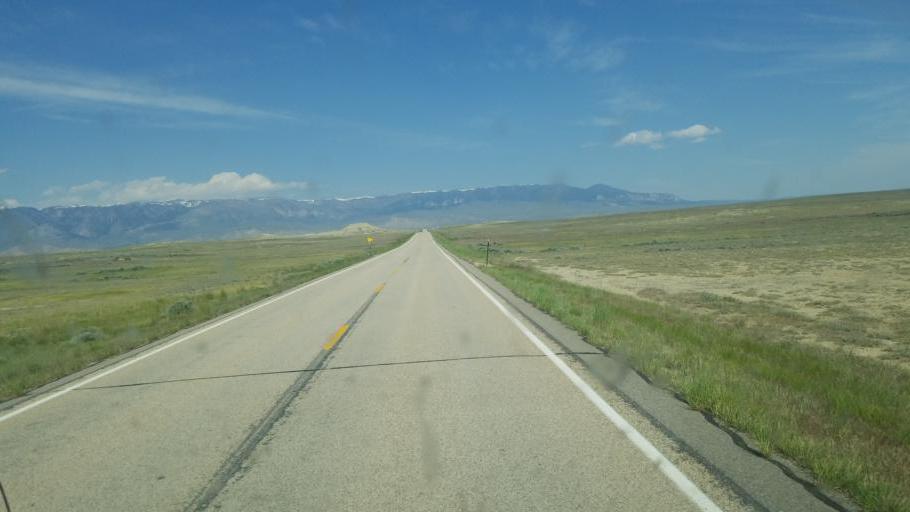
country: US
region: Wyoming
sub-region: Park County
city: Powell
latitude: 44.8753
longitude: -109.0542
